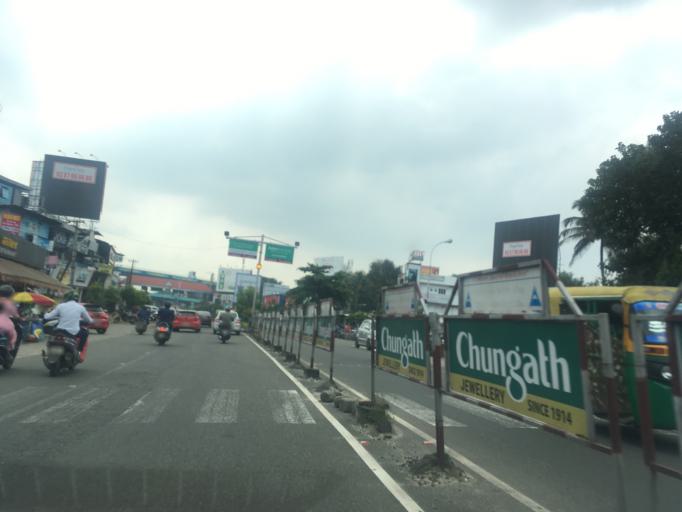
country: IN
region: Kerala
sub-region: Ernakulam
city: Elur
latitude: 10.0270
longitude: 76.3061
